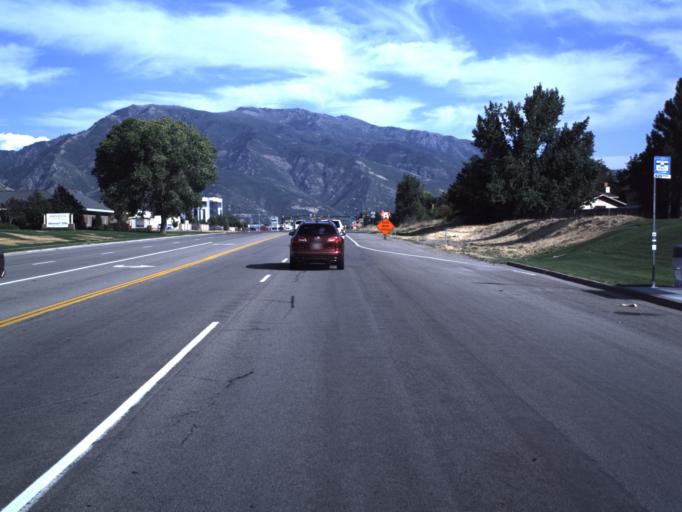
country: US
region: Utah
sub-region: Weber County
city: Uintah
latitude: 41.1585
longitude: -111.9442
